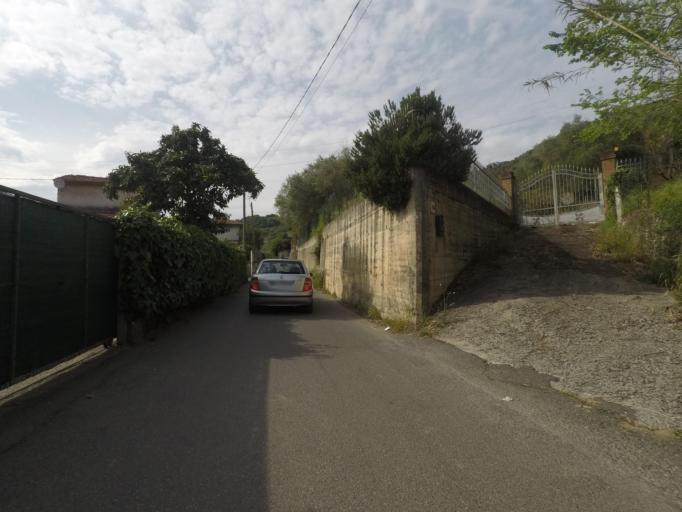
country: IT
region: Tuscany
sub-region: Provincia di Massa-Carrara
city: Massa
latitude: 44.0444
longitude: 10.1050
